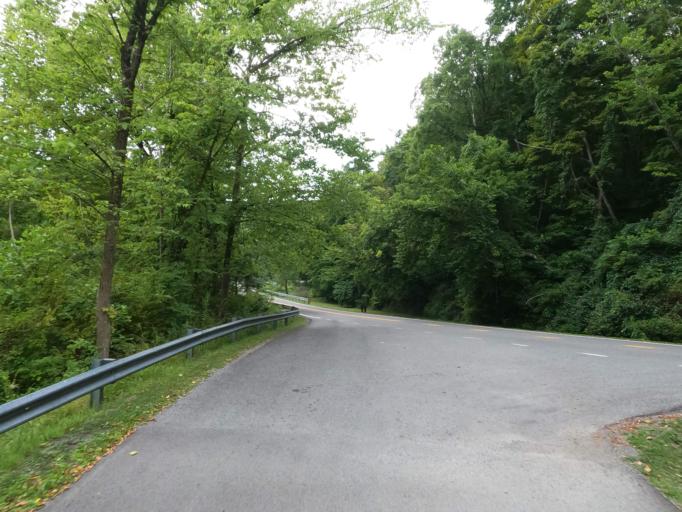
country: US
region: West Virginia
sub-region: Marion County
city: Fairmont
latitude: 39.5153
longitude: -80.0979
